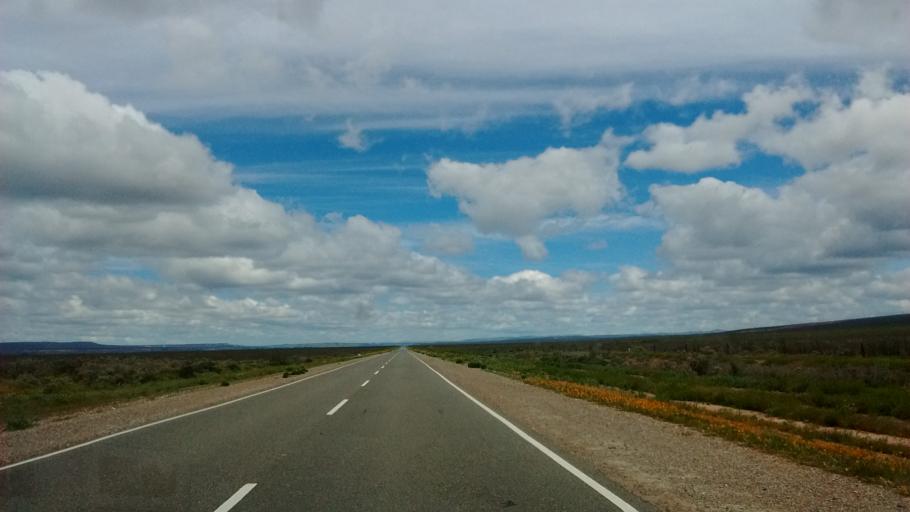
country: AR
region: Neuquen
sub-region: Departamento de Picun Leufu
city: Picun Leufu
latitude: -39.7895
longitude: -69.6712
